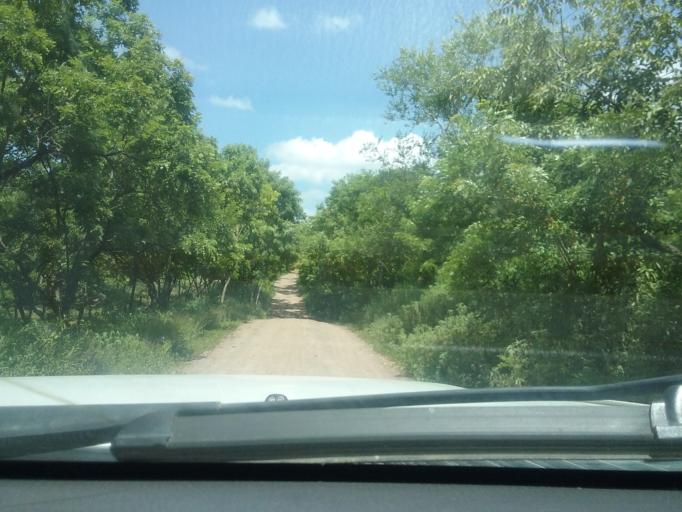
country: NI
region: Matagalpa
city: Terrabona
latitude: 12.6791
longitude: -85.9698
